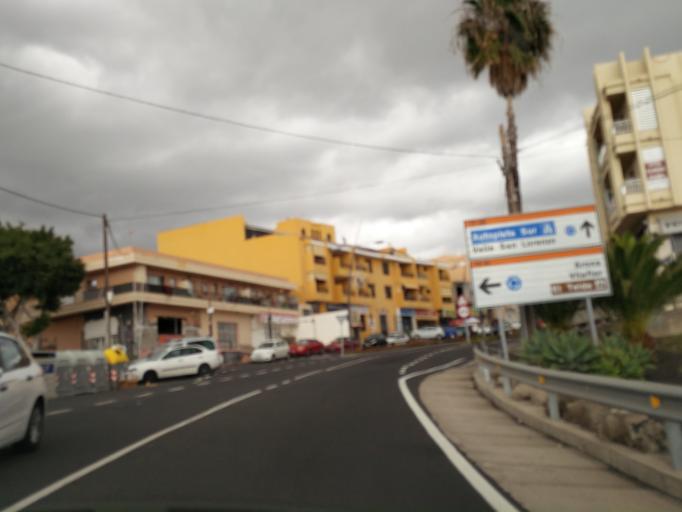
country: ES
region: Canary Islands
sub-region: Provincia de Santa Cruz de Tenerife
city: Arona
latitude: 28.0789
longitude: -16.6842
